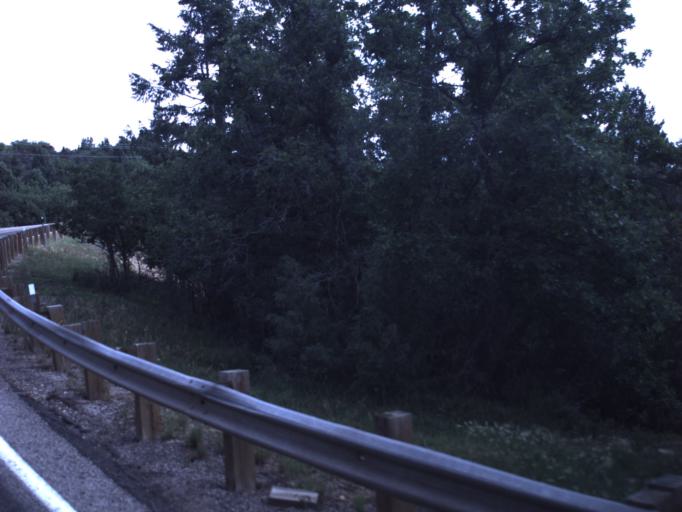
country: US
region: Utah
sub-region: Garfield County
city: Panguitch
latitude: 37.4912
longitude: -112.5311
